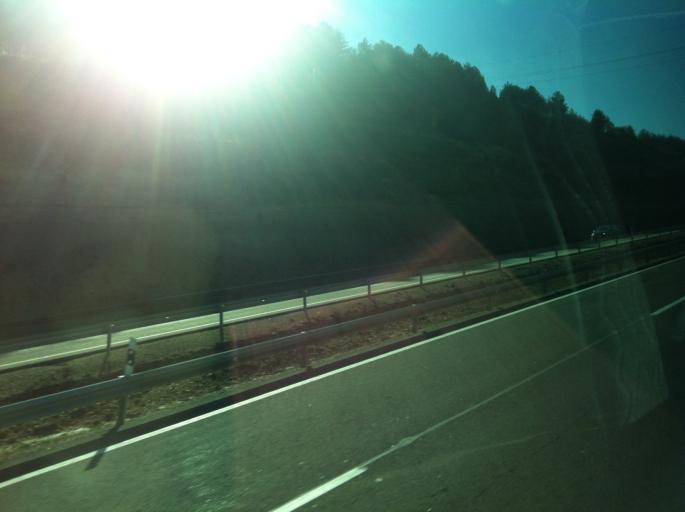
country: ES
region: Castille and Leon
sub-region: Provincia de Burgos
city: Fresno de Rodilla
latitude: 42.4438
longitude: -3.4890
